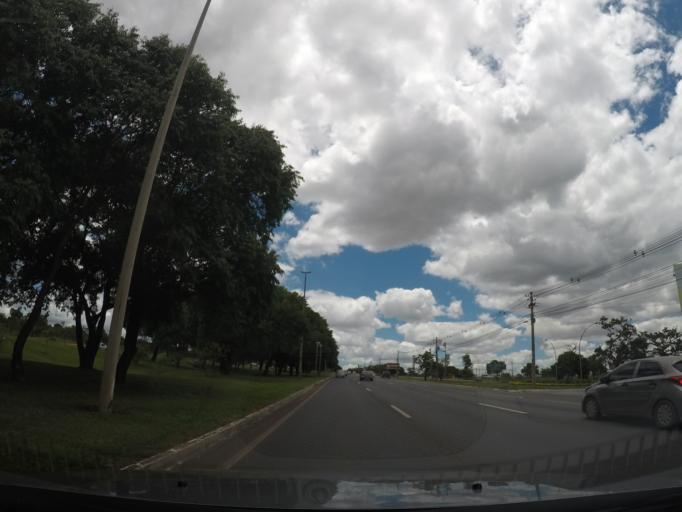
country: BR
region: Federal District
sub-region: Brasilia
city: Brasilia
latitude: -15.7515
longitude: -47.9242
